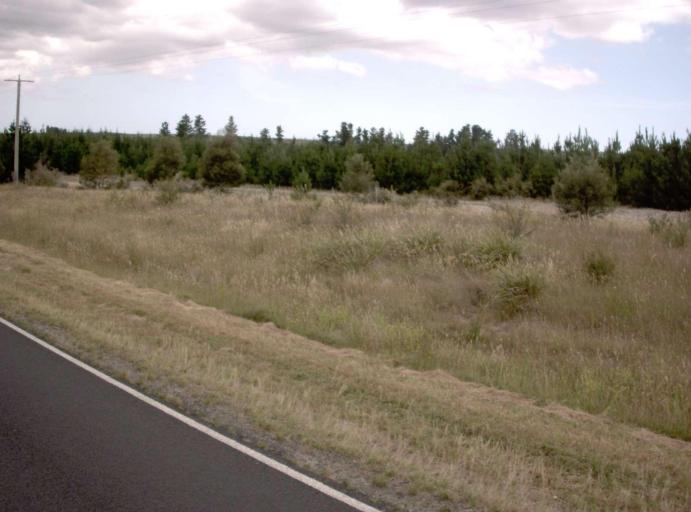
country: AU
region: Victoria
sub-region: Wellington
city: Sale
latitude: -38.1726
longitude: 147.0149
